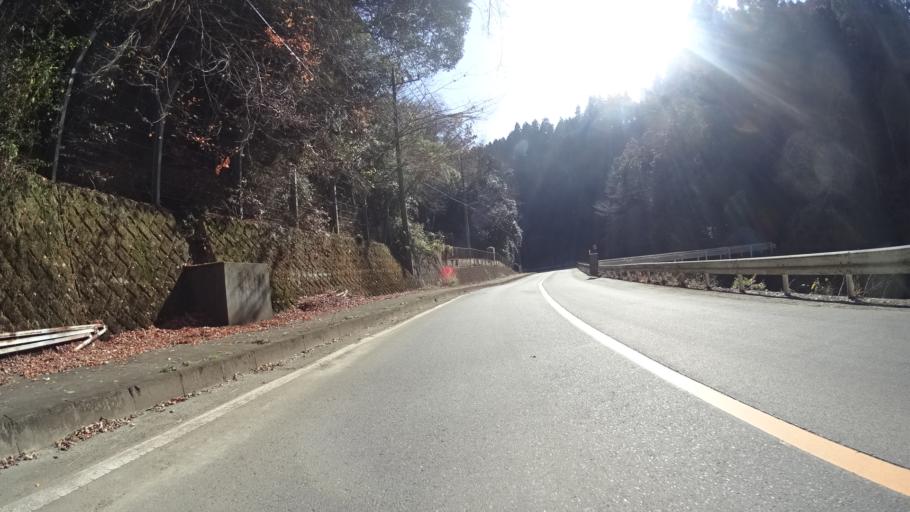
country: JP
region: Yamanashi
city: Uenohara
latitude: 35.6310
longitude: 139.1444
